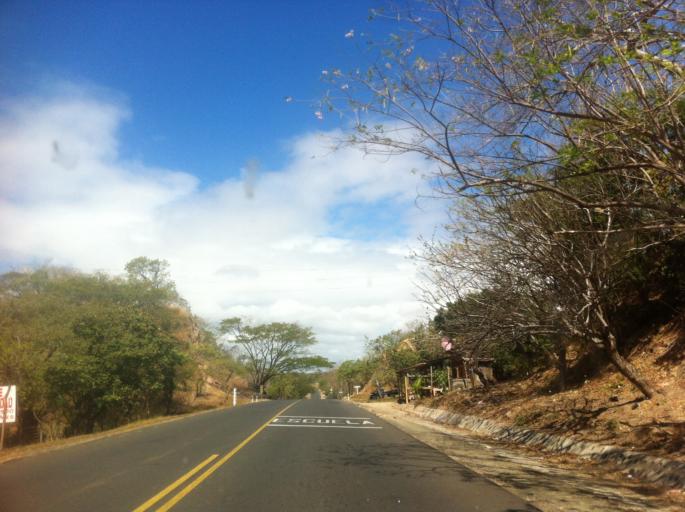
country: NI
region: Chontales
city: Acoyapa
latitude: 12.0115
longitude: -85.2426
